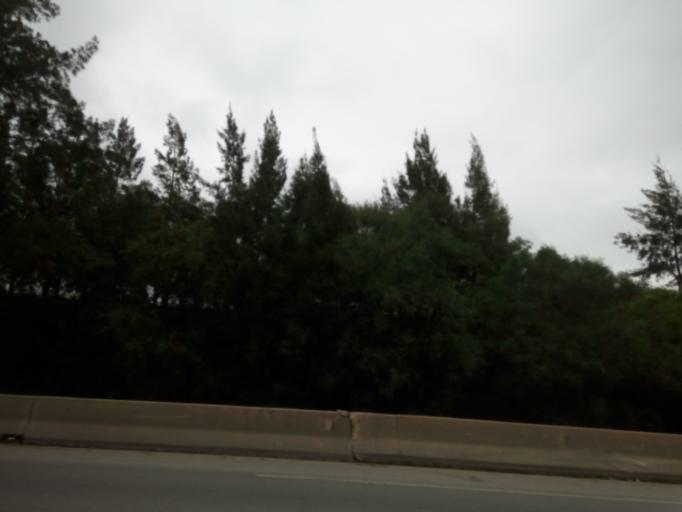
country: DZ
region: Blida
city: Chiffa
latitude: 36.4690
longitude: 2.7672
